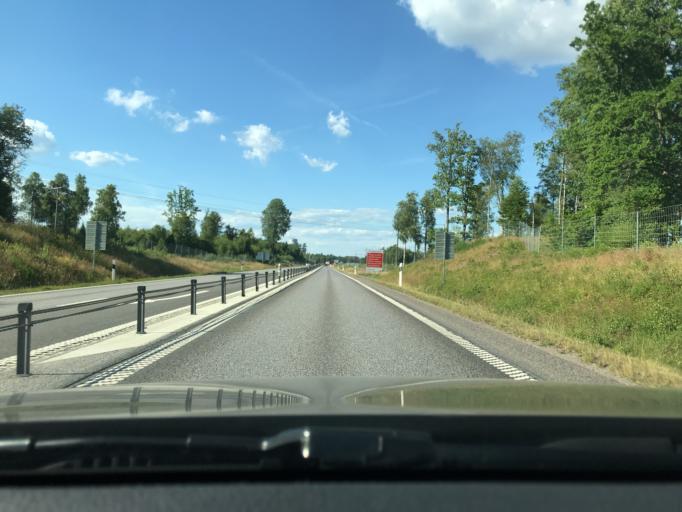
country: SE
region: Kronoberg
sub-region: Almhults Kommun
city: AElmhult
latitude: 56.5242
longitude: 14.1407
